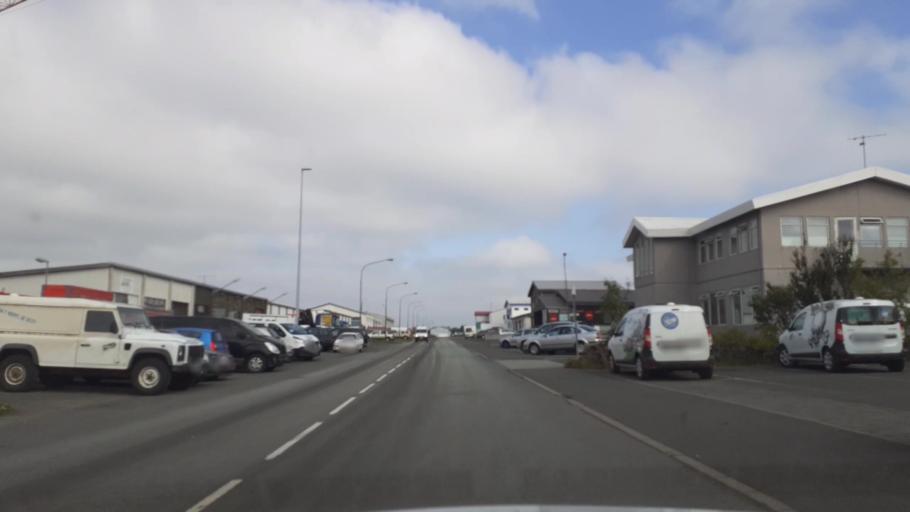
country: IS
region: Capital Region
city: Hafnarfjoerdur
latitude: 64.0775
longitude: -21.9356
